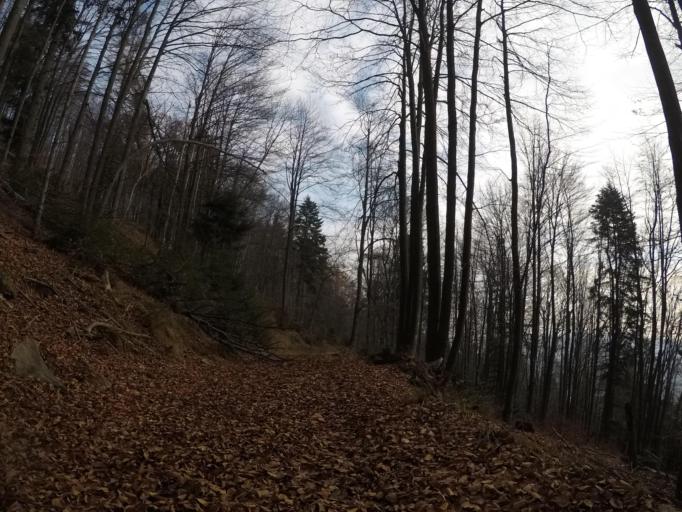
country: SK
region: Kosicky
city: Gelnica
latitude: 48.7743
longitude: 20.9529
